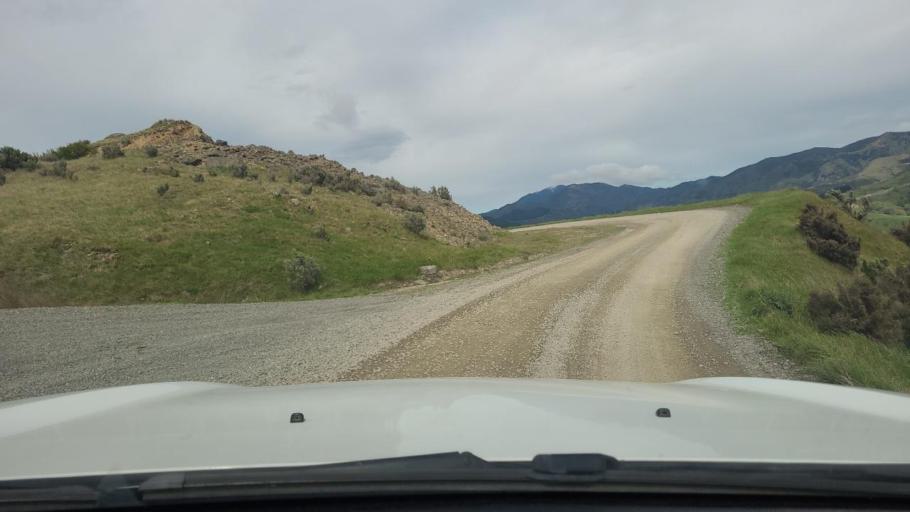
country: NZ
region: Wellington
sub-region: South Wairarapa District
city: Waipawa
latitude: -41.3798
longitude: 175.4684
